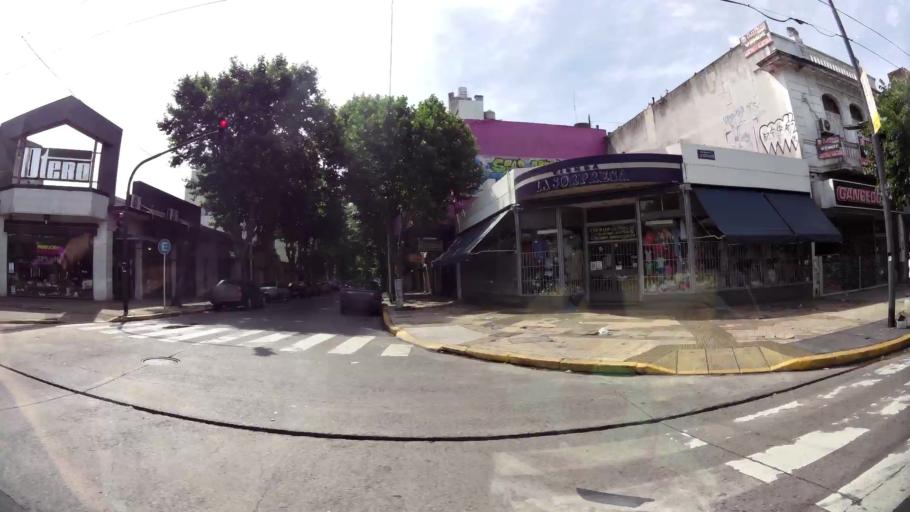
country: AR
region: Buenos Aires F.D.
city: Villa Lugano
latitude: -34.6544
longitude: -58.5057
